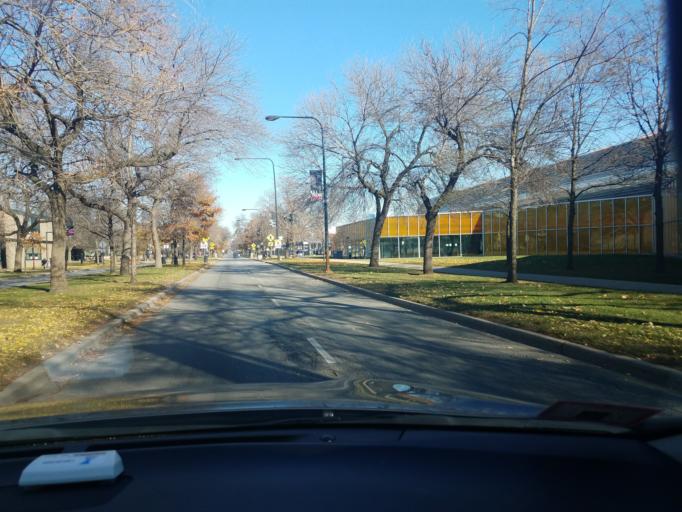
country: US
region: Illinois
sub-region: Cook County
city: Chicago
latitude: 41.8354
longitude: -87.6265
